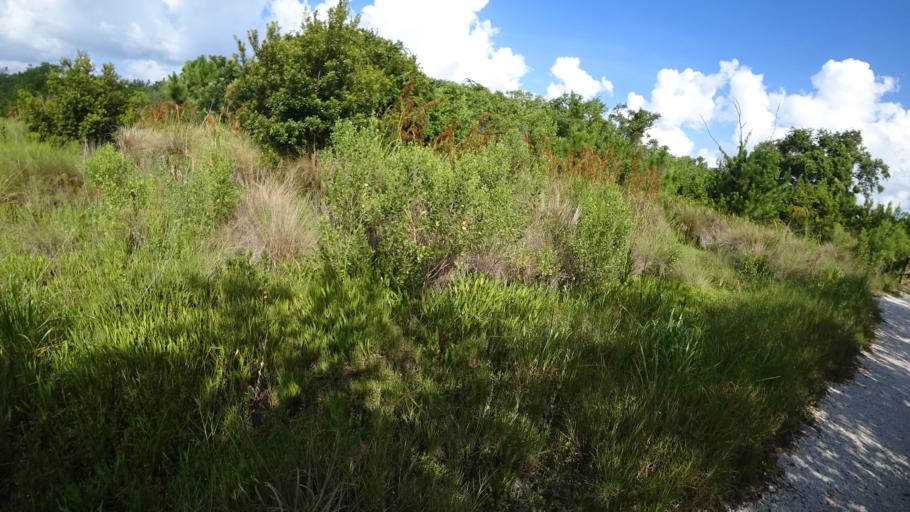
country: US
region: Florida
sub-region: Manatee County
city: Cortez
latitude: 27.4976
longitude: -82.6781
